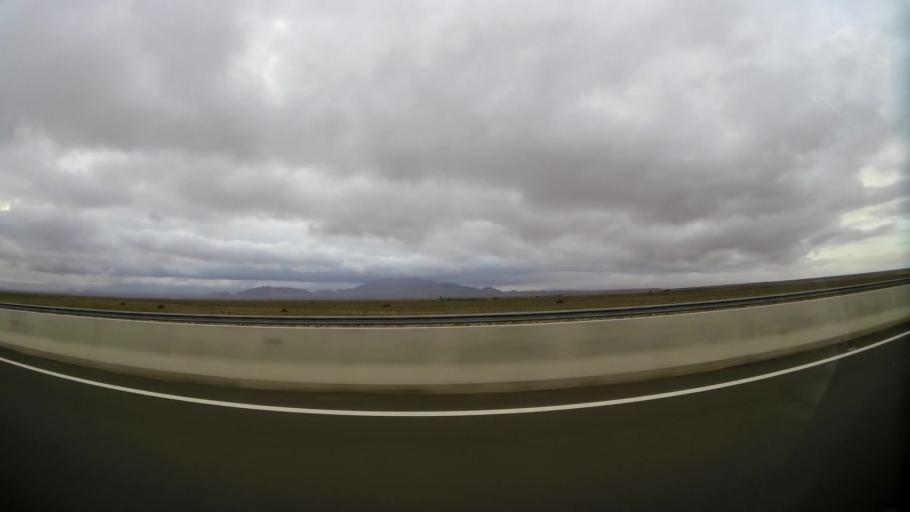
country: MA
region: Taza-Al Hoceima-Taounate
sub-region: Taza
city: Guercif
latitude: 34.3785
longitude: -3.2473
